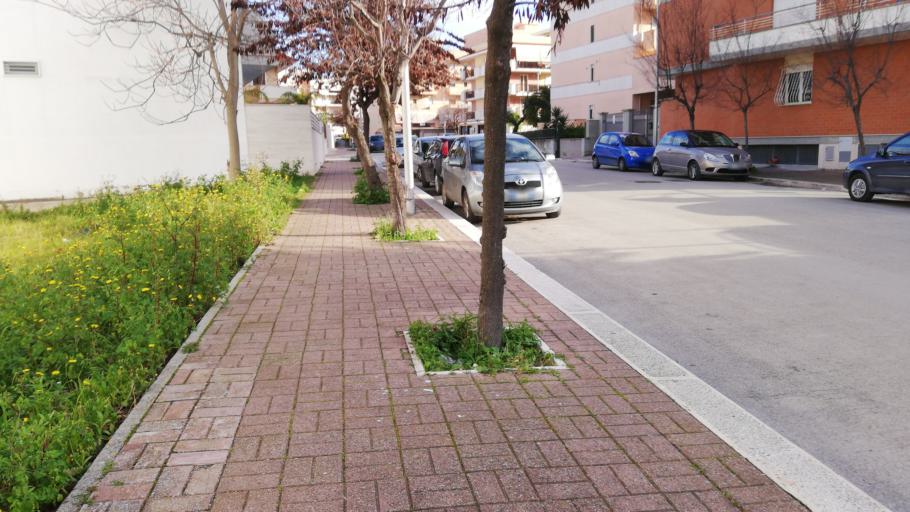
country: IT
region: Apulia
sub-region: Provincia di Barletta - Andria - Trani
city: Andria
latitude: 41.2380
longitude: 16.2964
